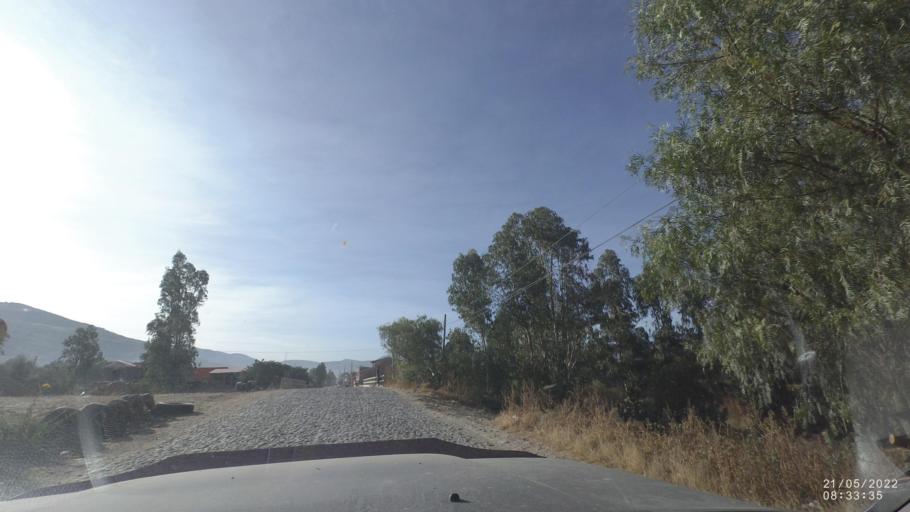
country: BO
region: Cochabamba
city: Cochabamba
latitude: -17.3863
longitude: -66.0497
